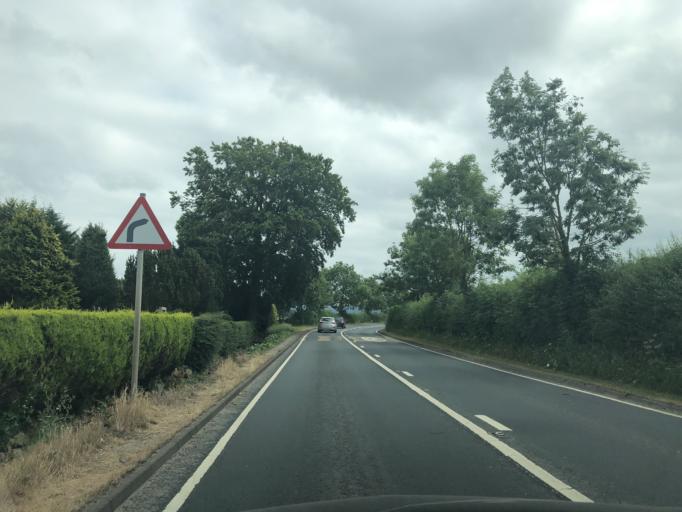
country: GB
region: England
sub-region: North Yorkshire
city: Great Ayton
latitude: 54.4856
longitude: -1.1441
